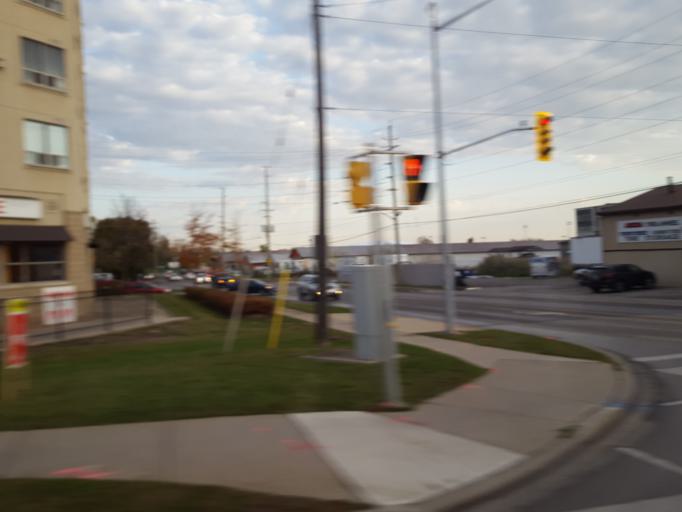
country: CA
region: Ontario
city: Newmarket
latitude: 44.0021
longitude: -79.4570
